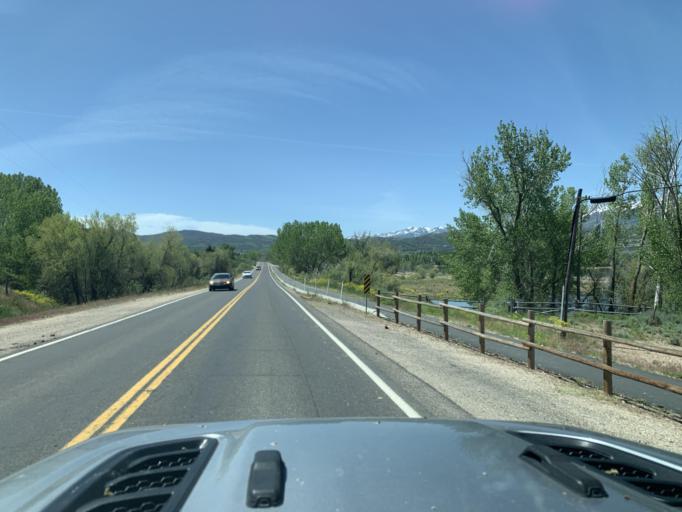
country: US
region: Utah
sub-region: Weber County
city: Wolf Creek
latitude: 41.2764
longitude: -111.7771
